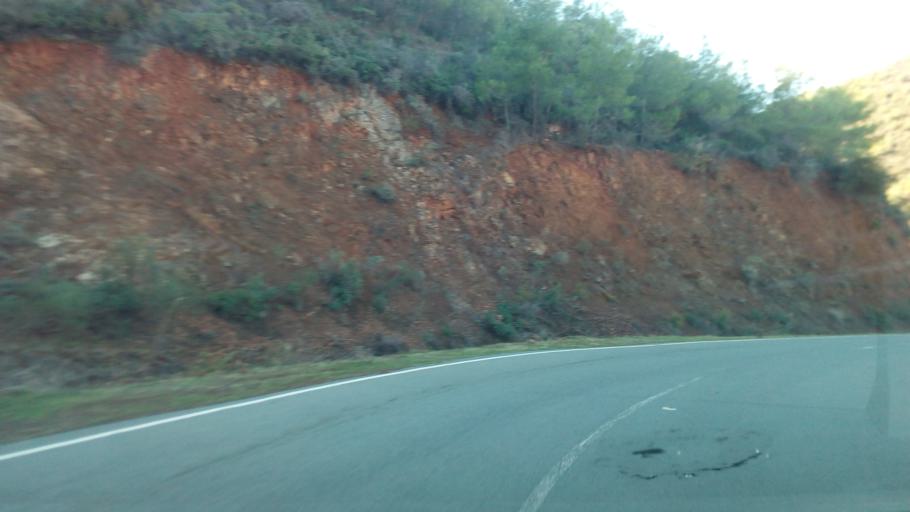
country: CY
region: Lefkosia
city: Kato Pyrgos
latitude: 35.1056
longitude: 32.7478
